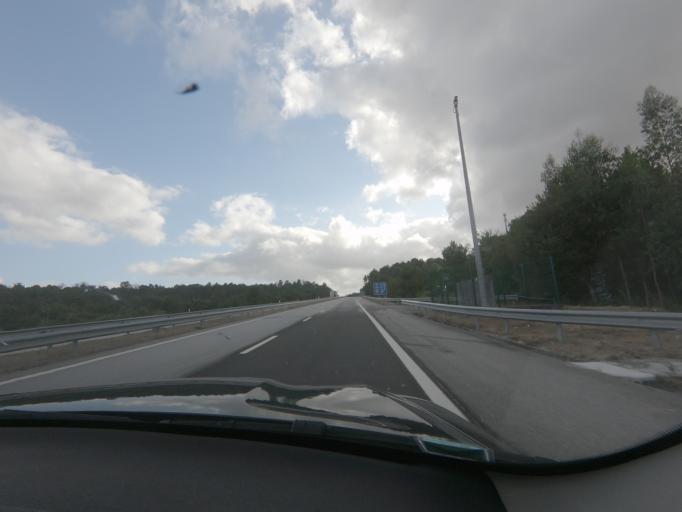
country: PT
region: Viseu
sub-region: Viseu
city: Abraveses
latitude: 40.7007
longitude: -7.9544
